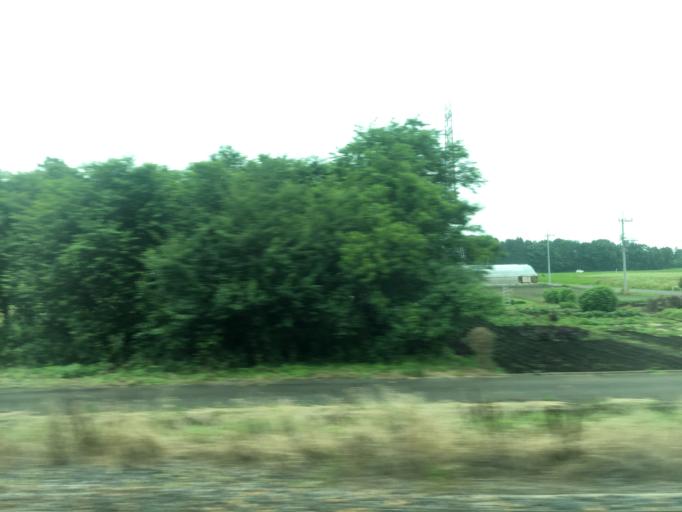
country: JP
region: Tochigi
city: Oyama
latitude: 36.3572
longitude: 139.8321
